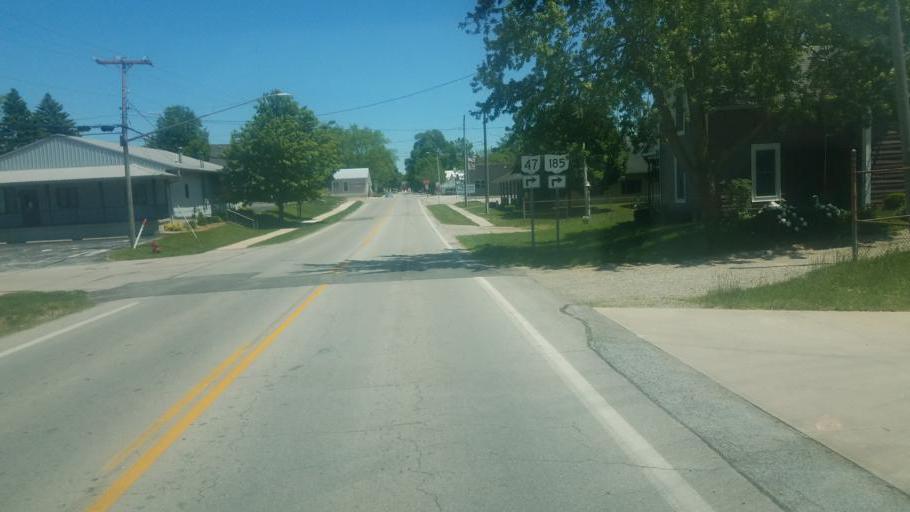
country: US
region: Ohio
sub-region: Darke County
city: Versailles
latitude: 40.2258
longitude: -84.4891
